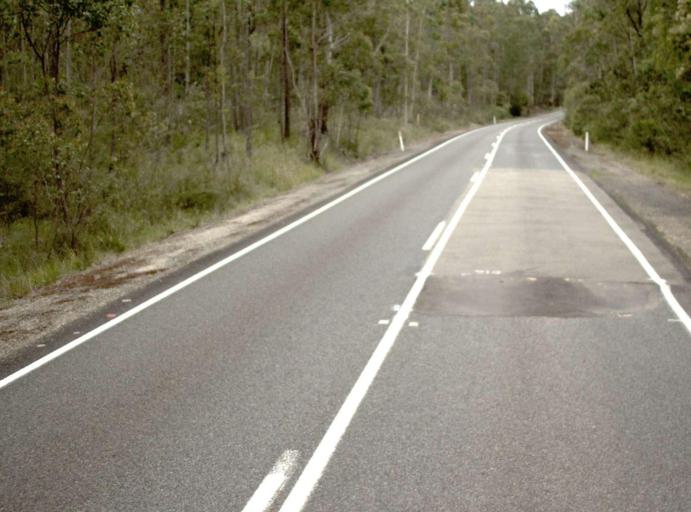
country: AU
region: New South Wales
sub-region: Bombala
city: Bombala
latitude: -37.2796
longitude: 149.2235
